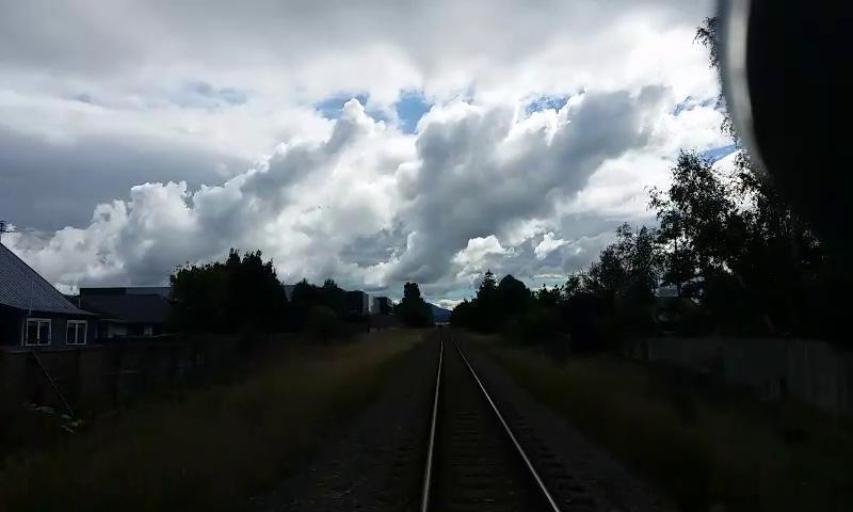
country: NZ
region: Canterbury
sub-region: Waimakariri District
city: Woodend
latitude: -43.3087
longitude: 172.5997
